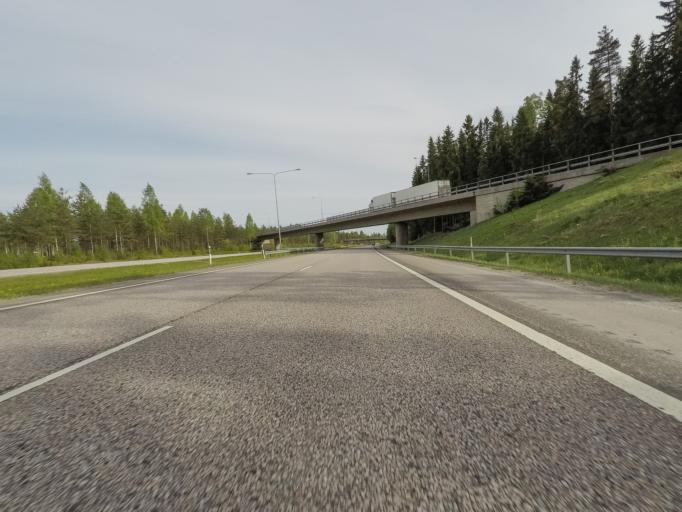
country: FI
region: Uusimaa
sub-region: Helsinki
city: Hyvinge
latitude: 60.5538
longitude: 24.8330
